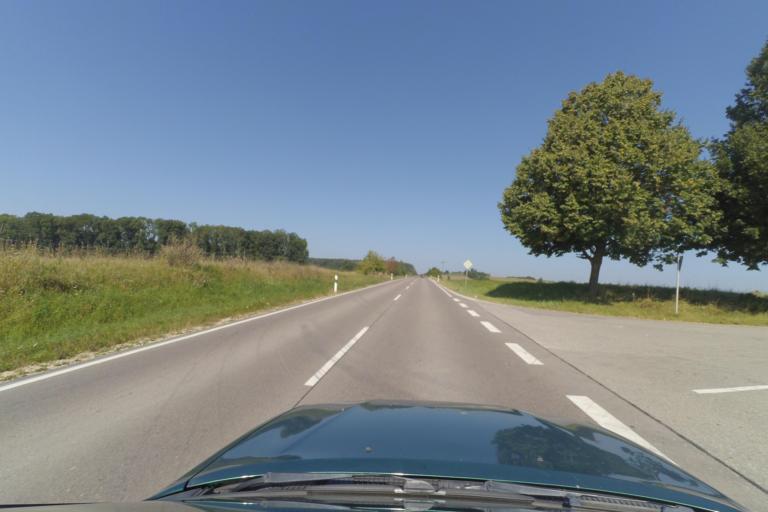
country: DE
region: Bavaria
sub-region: Swabia
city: Wittislingen
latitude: 48.6084
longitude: 10.4069
